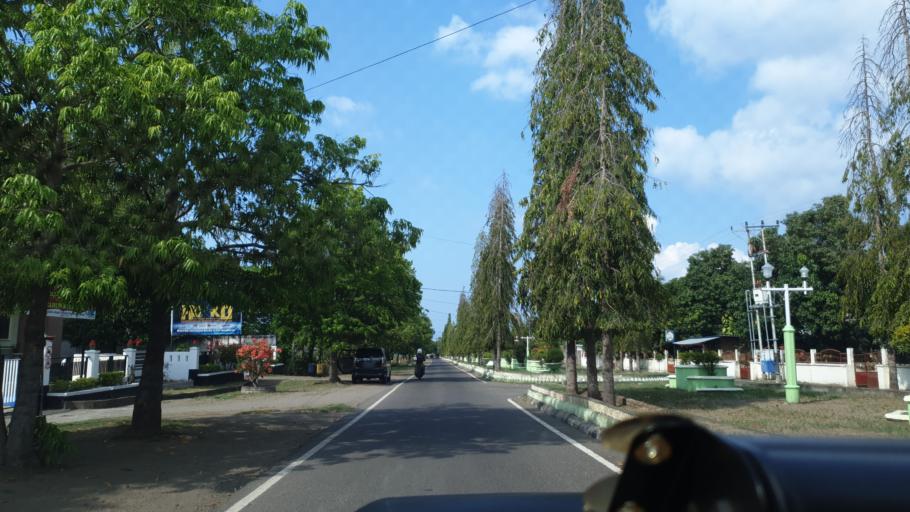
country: ID
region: East Nusa Tenggara
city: Waioti
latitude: -8.6330
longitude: 122.2360
